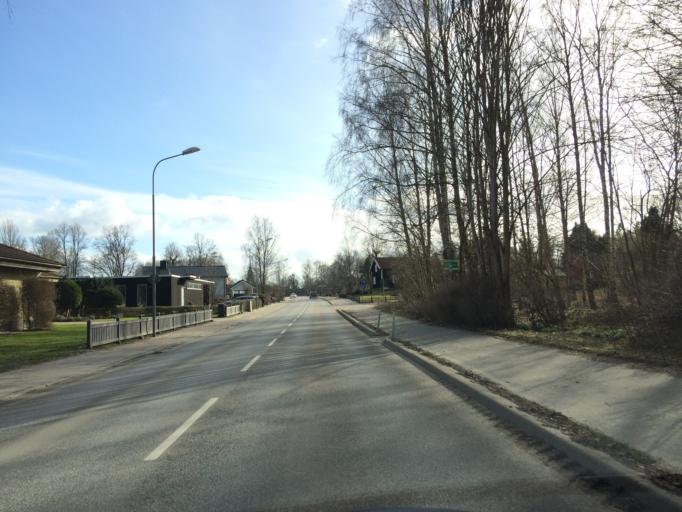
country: SE
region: Kronoberg
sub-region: Almhults Kommun
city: AElmhult
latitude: 56.5581
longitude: 14.1303
